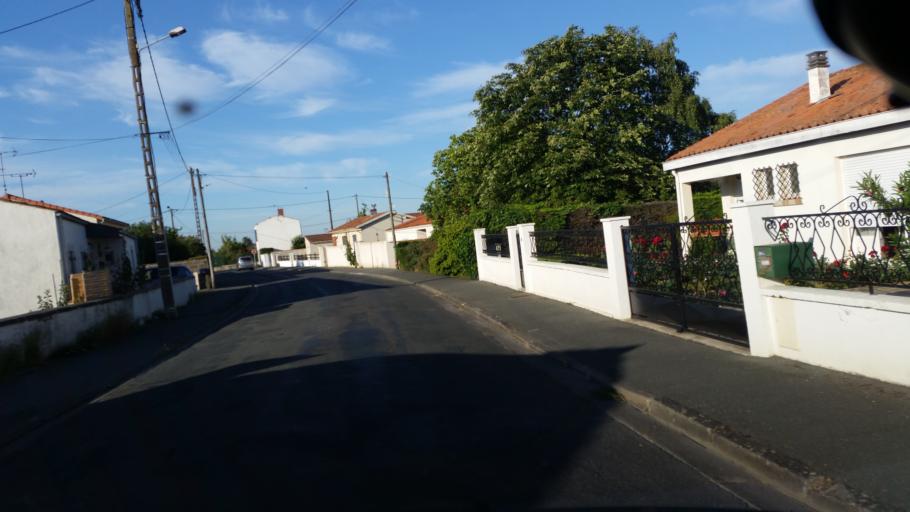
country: FR
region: Poitou-Charentes
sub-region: Departement de la Charente-Maritime
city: Marans
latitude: 46.3048
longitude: -0.9936
